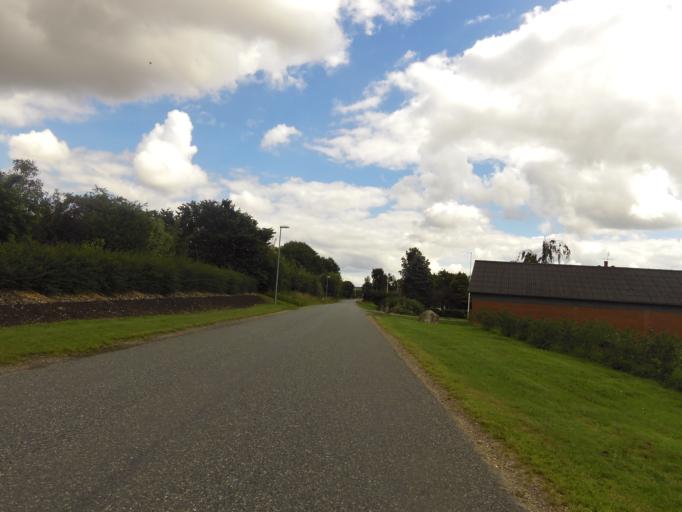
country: DK
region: South Denmark
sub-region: Haderslev Kommune
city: Vojens
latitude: 55.2855
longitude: 9.3384
